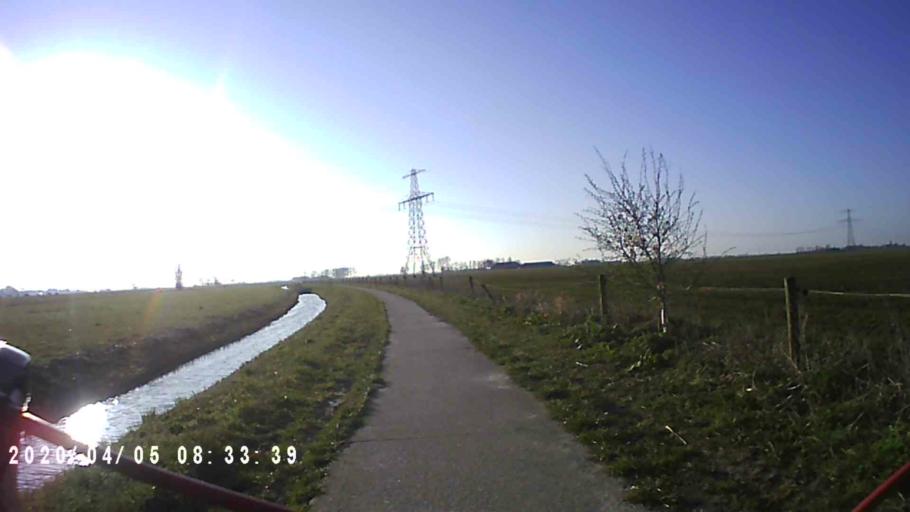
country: NL
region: Groningen
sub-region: Gemeente Winsum
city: Winsum
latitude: 53.3259
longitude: 6.4912
